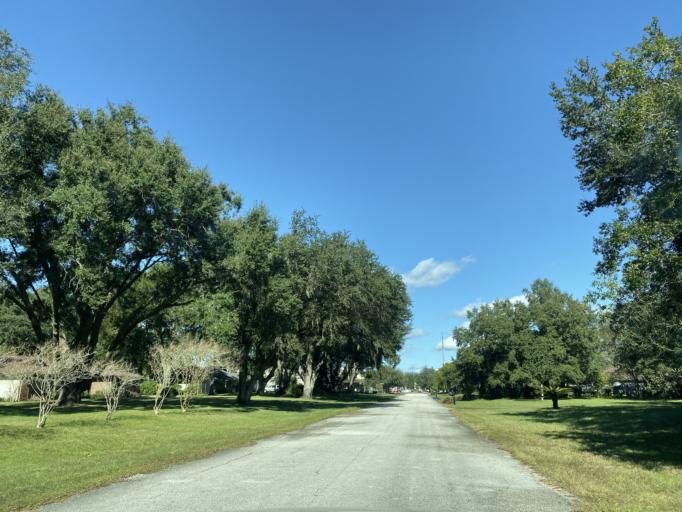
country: US
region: Florida
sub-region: Seminole County
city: Goldenrod
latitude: 28.6166
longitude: -81.2556
